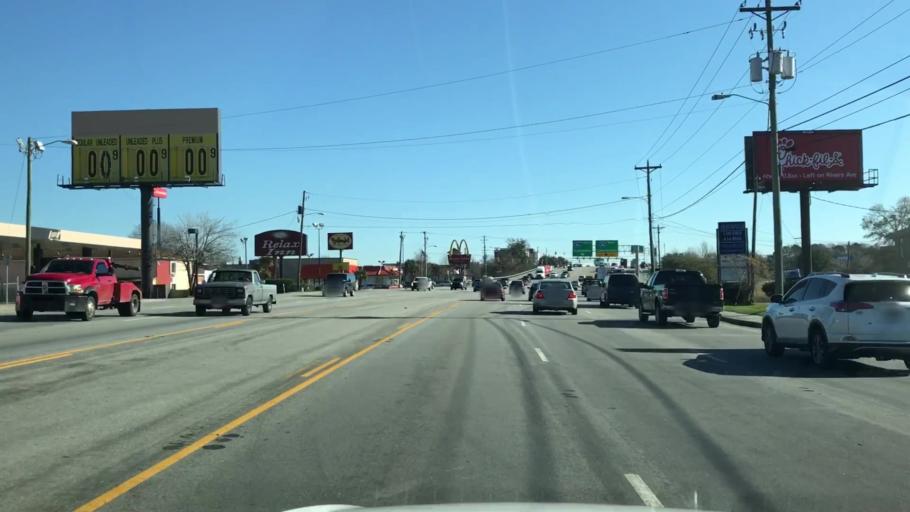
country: US
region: South Carolina
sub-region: Berkeley County
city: Hanahan
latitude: 32.9337
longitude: -80.0522
